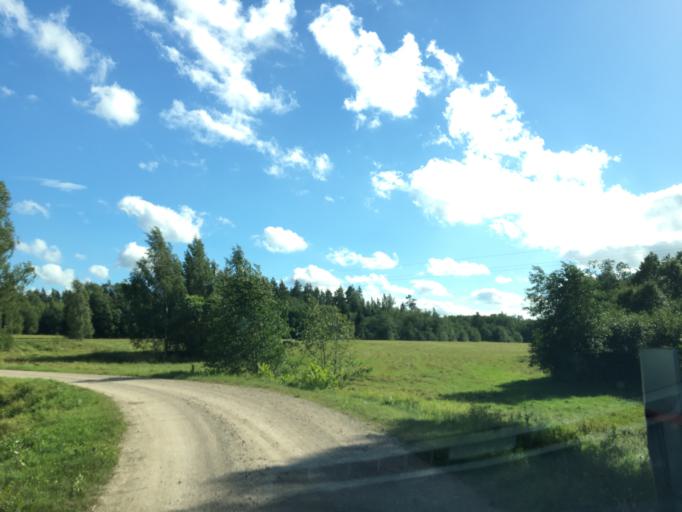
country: EE
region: Viljandimaa
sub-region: Suure-Jaani vald
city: Suure-Jaani
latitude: 58.5803
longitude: 25.2721
